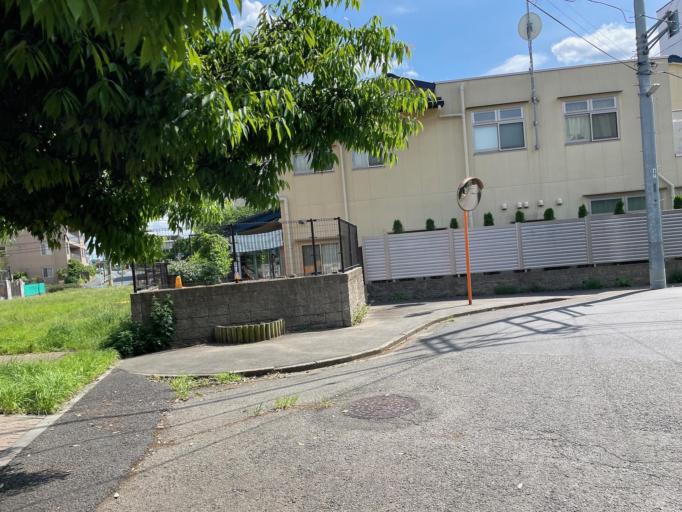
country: JP
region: Tokyo
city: Mitaka-shi
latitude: 35.6643
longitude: 139.6237
